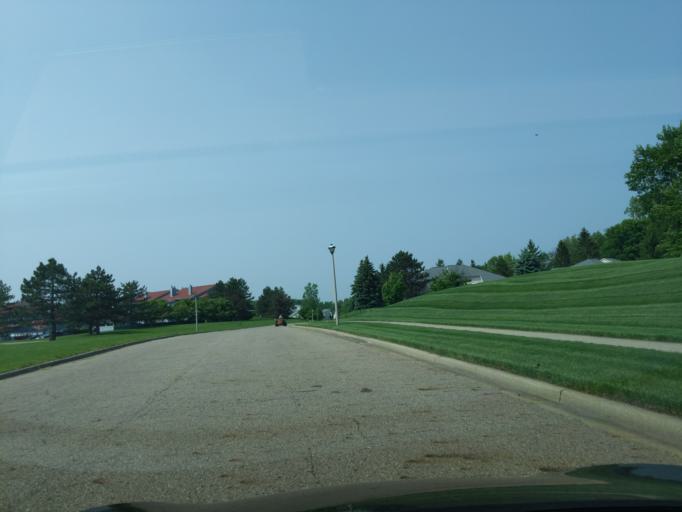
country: US
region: Michigan
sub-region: Eaton County
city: Waverly
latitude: 42.7462
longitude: -84.6542
